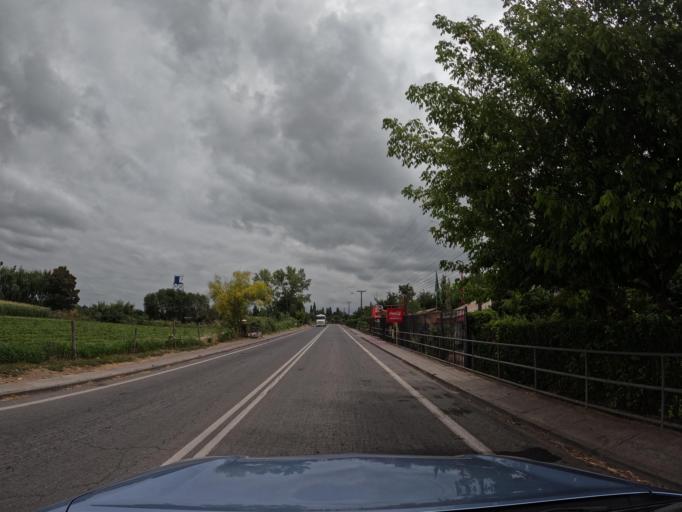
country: CL
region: Maule
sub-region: Provincia de Curico
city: Teno
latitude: -34.7528
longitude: -71.2387
